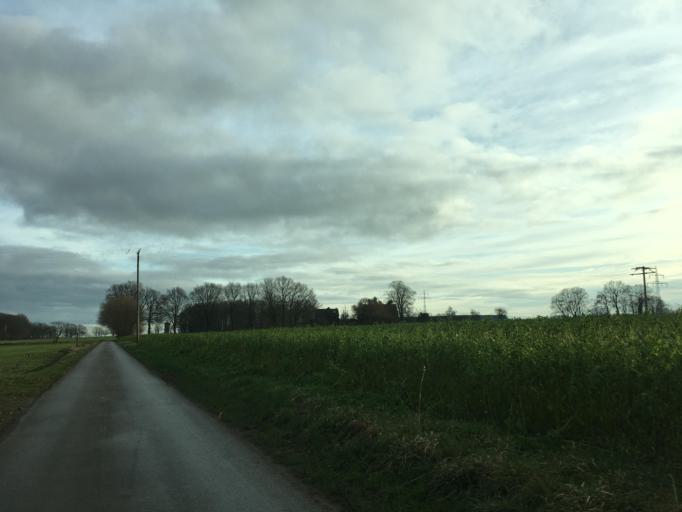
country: DE
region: North Rhine-Westphalia
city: Ludinghausen
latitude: 51.7890
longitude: 7.3725
